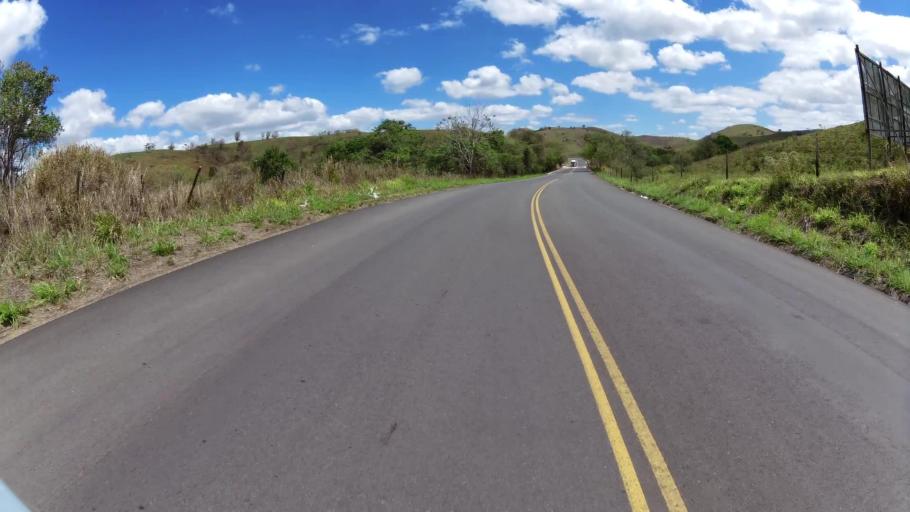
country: BR
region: Rio de Janeiro
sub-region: Itaperuna
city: Itaperuna
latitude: -21.3292
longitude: -41.8781
